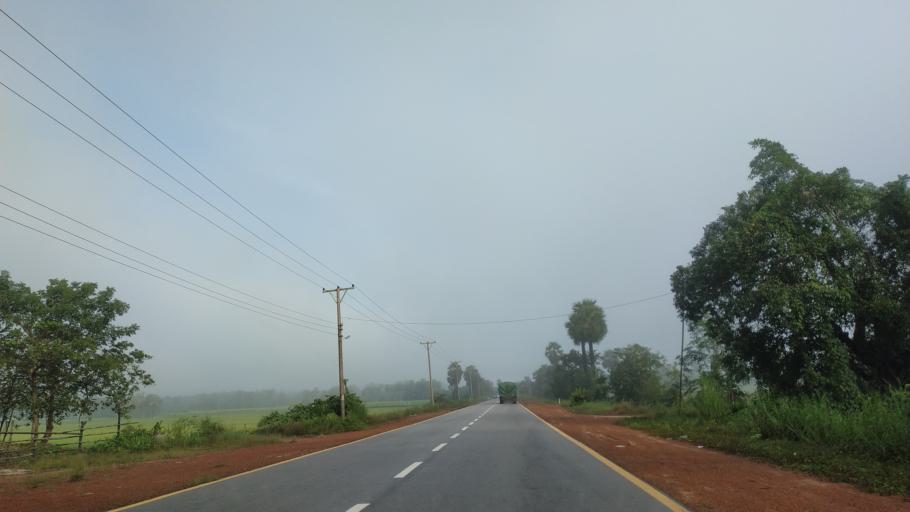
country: MM
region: Tanintharyi
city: Dawei
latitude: 14.1889
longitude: 98.2049
